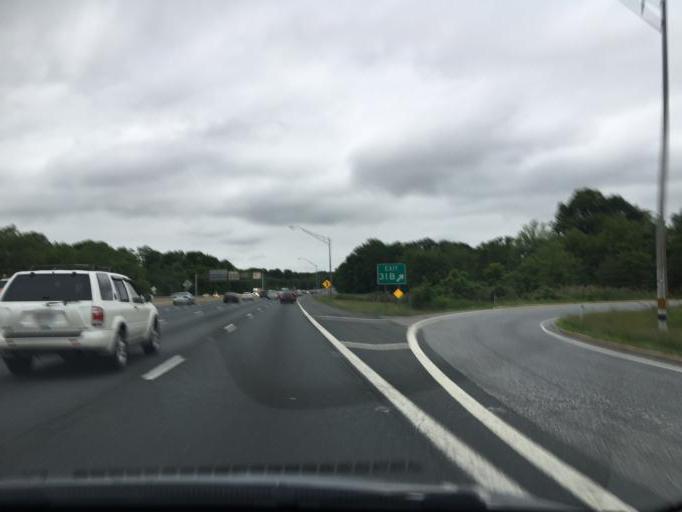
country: US
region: Maryland
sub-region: Baltimore County
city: Carney
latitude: 39.3879
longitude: -76.5297
